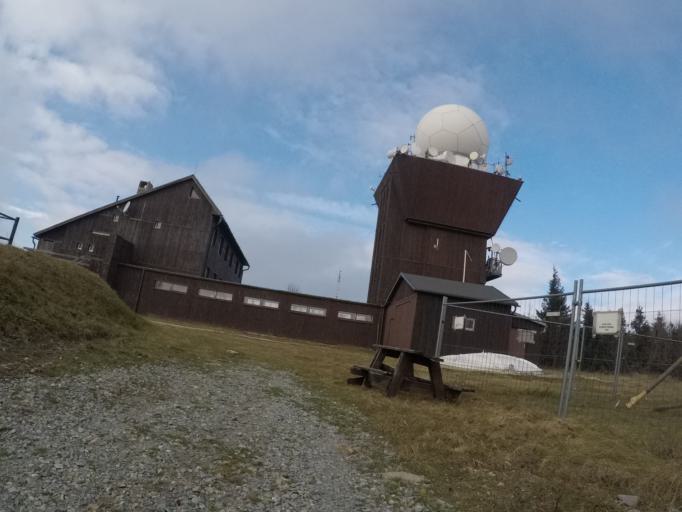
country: SK
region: Kosicky
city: Gelnica
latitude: 48.7826
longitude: 20.9875
